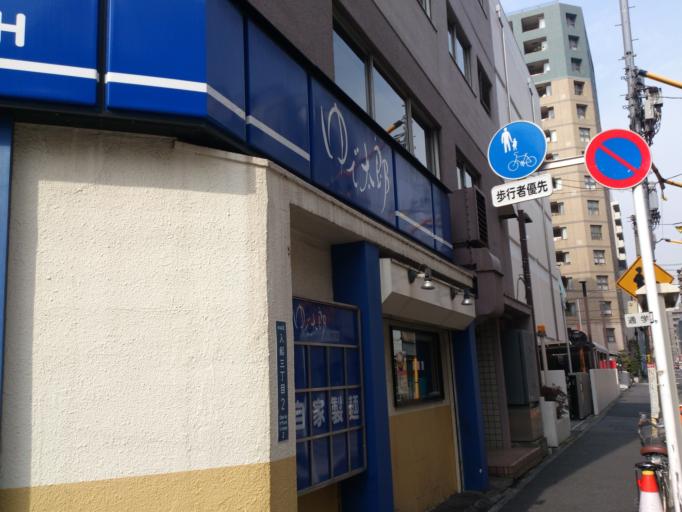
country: JP
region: Tokyo
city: Tokyo
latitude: 35.6701
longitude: 139.7760
